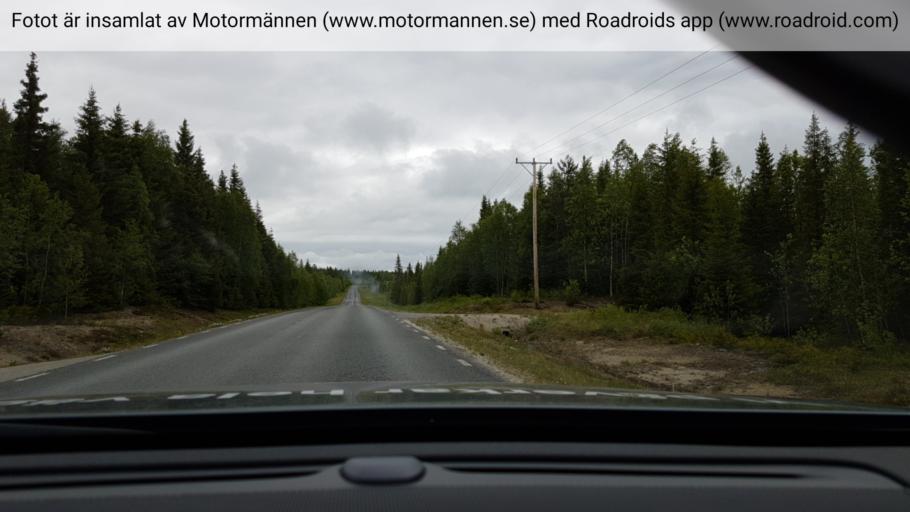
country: SE
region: Vaesterbotten
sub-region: Lycksele Kommun
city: Soderfors
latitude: 64.3749
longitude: 17.9752
